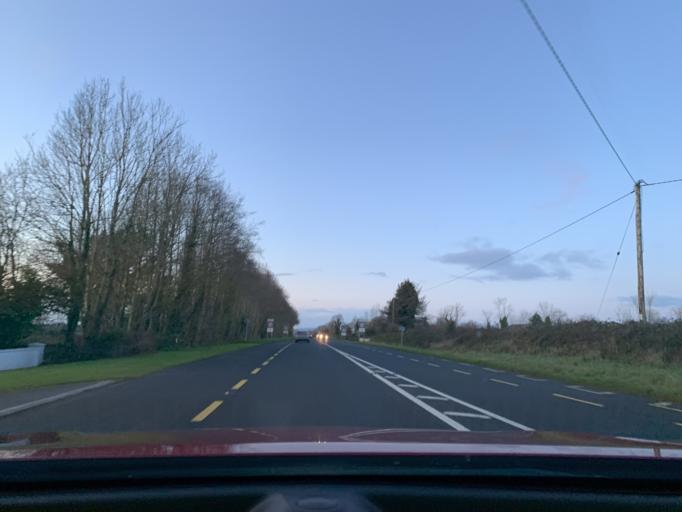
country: IE
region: Connaught
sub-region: County Leitrim
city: Carrick-on-Shannon
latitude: 53.8975
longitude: -7.9528
